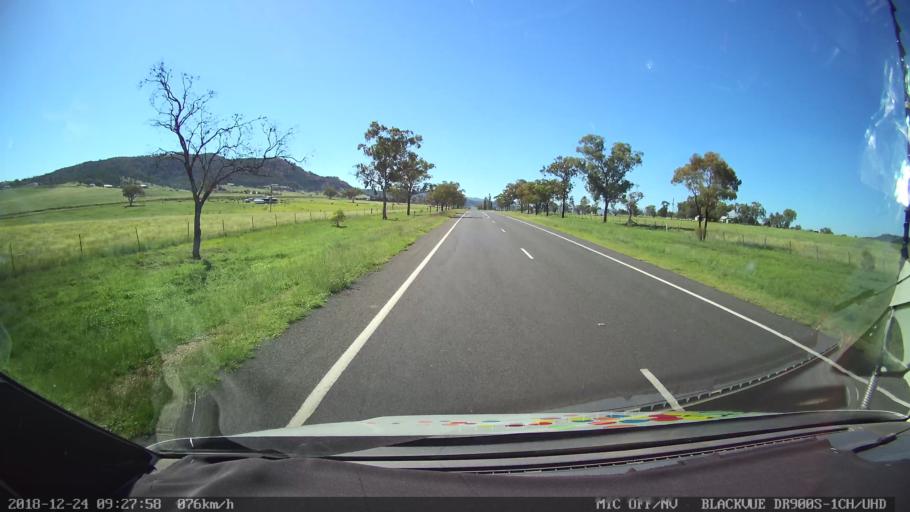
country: AU
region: New South Wales
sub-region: Liverpool Plains
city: Quirindi
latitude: -31.5330
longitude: 150.6849
